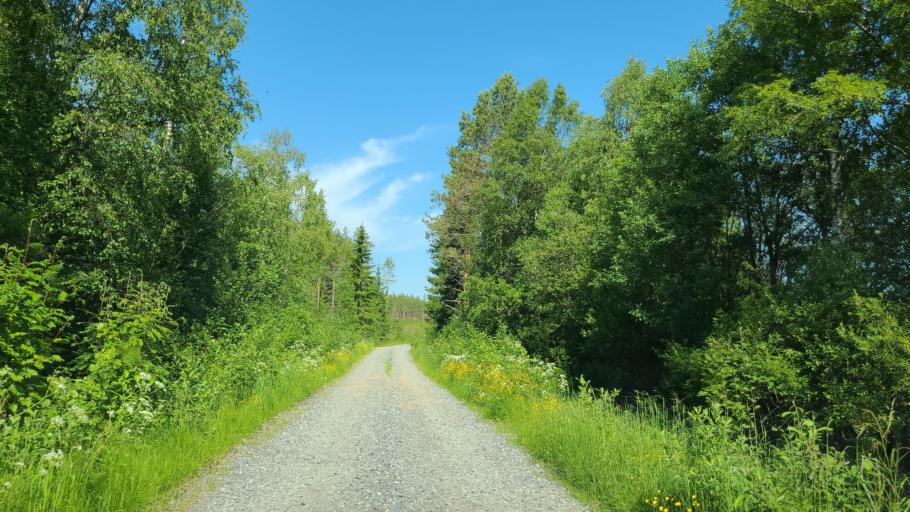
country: SE
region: Vaesterbotten
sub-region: Robertsfors Kommun
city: Robertsfors
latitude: 64.0906
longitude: 20.8366
